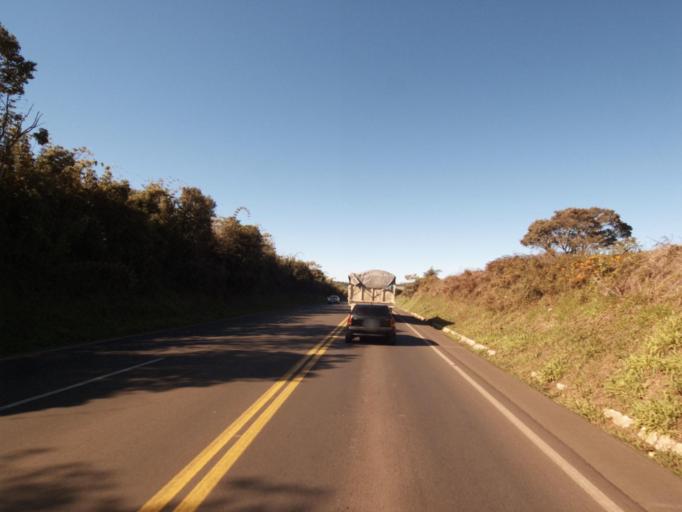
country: BR
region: Santa Catarina
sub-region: Xanxere
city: Xanxere
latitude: -26.9160
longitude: -52.4896
